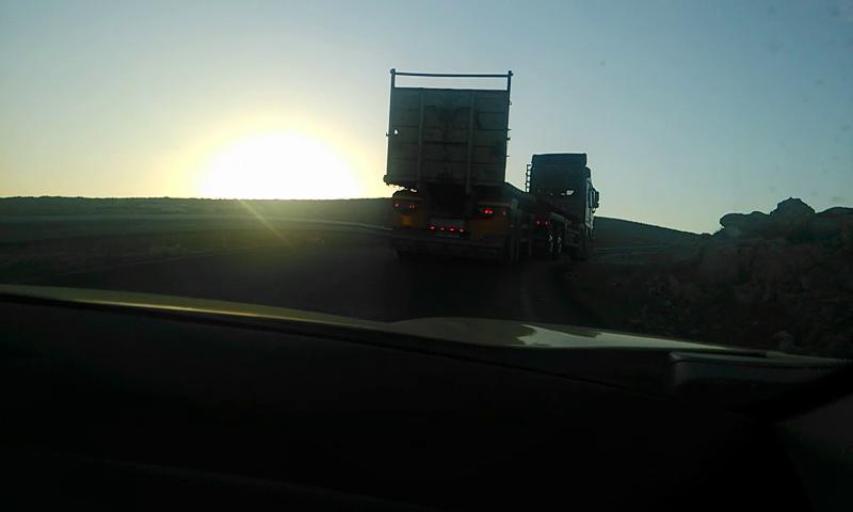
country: PS
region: West Bank
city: Rammun
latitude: 31.9153
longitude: 35.3504
